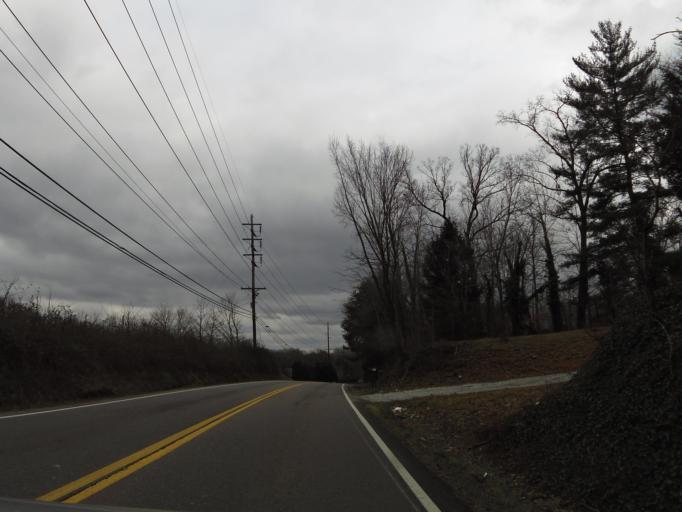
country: US
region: Tennessee
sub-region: Union County
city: Condon
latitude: 36.1184
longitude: -83.8706
